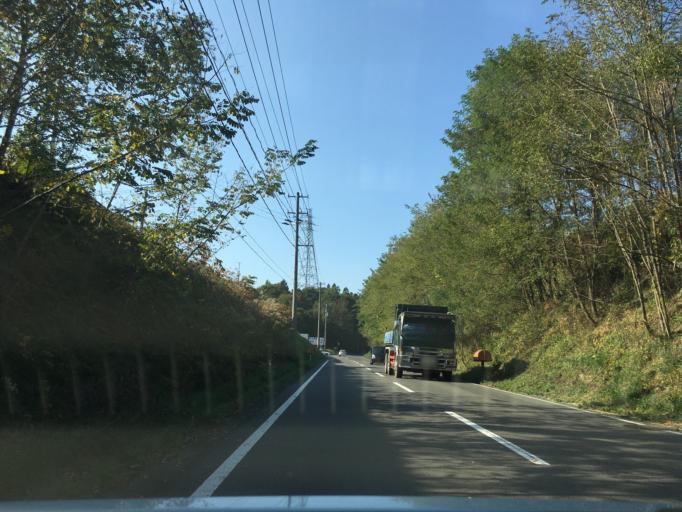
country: JP
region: Fukushima
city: Sukagawa
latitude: 37.2793
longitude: 140.2894
